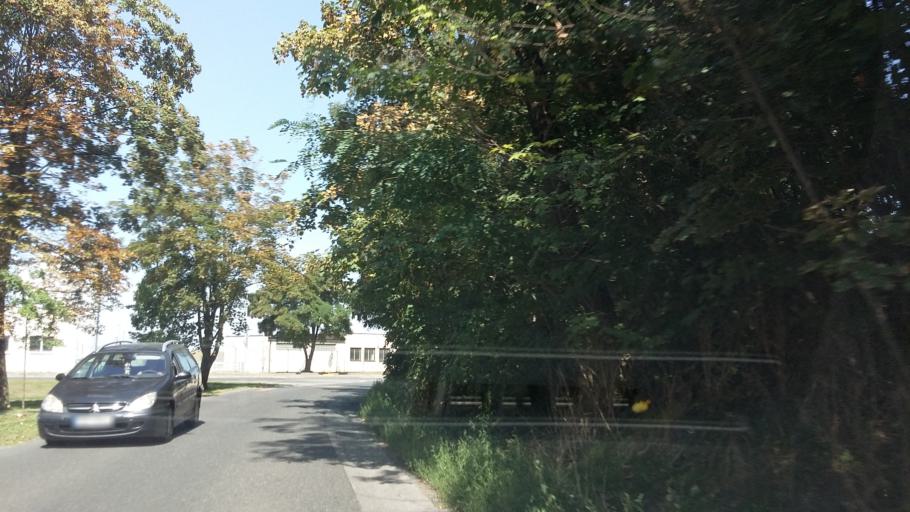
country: CZ
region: Central Bohemia
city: Zelenec
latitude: 50.1223
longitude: 14.6358
